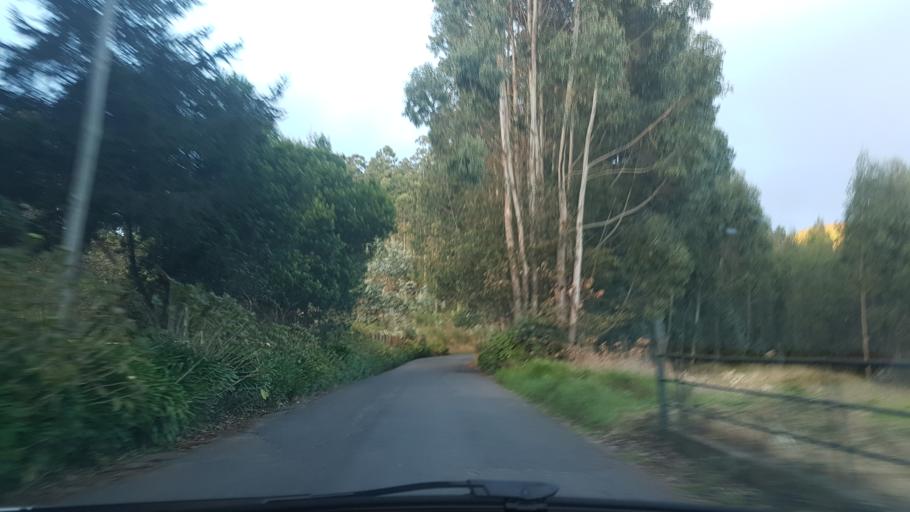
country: PT
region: Madeira
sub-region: Calheta
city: Arco da Calheta
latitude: 32.7267
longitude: -17.1097
